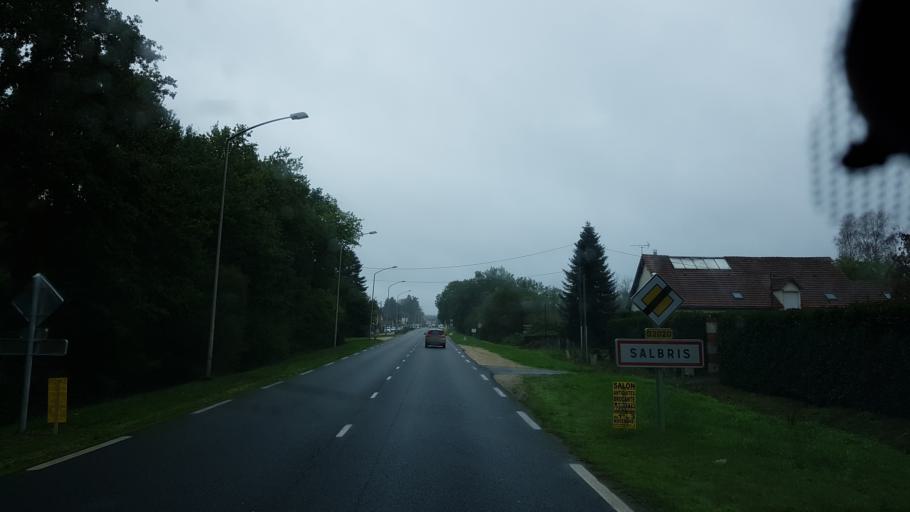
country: FR
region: Centre
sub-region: Departement du Loir-et-Cher
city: Salbris
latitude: 47.4366
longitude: 2.0485
